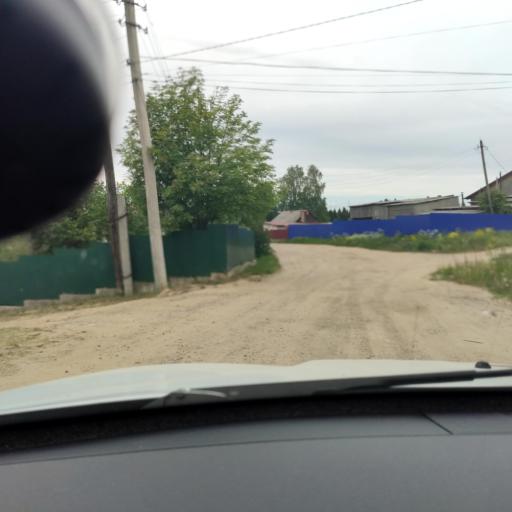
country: RU
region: Perm
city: Polazna
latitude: 58.3017
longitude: 56.3972
